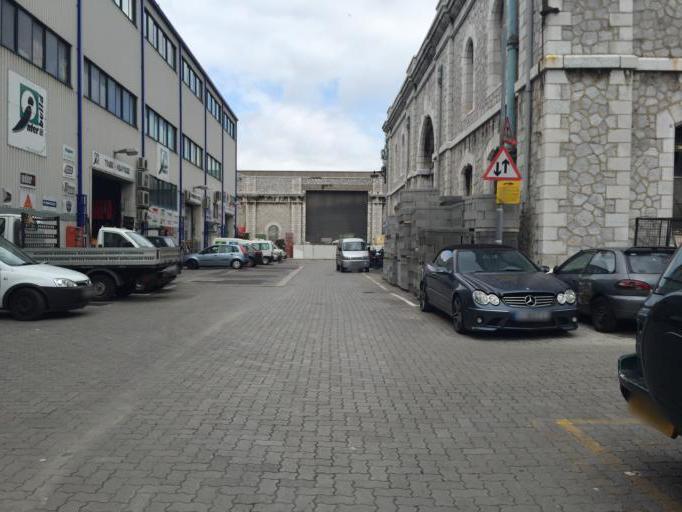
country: GI
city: Gibraltar
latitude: 36.1270
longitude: -5.3529
